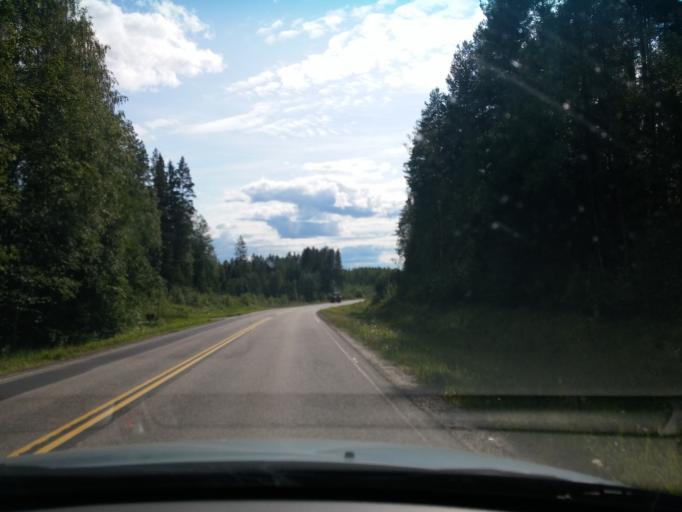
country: FI
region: Central Finland
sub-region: Keuruu
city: Keuruu
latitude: 62.2925
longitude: 24.7094
